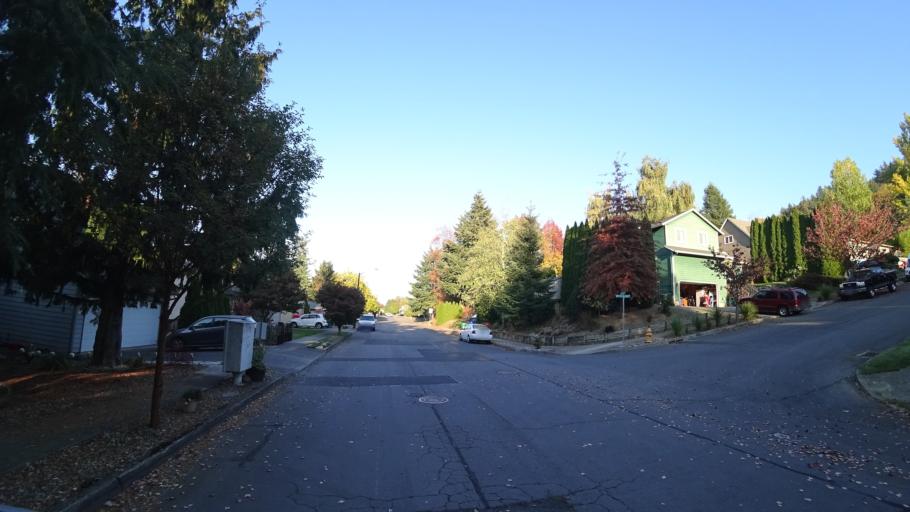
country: US
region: Oregon
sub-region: Multnomah County
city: Gresham
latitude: 45.4922
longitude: -122.4430
